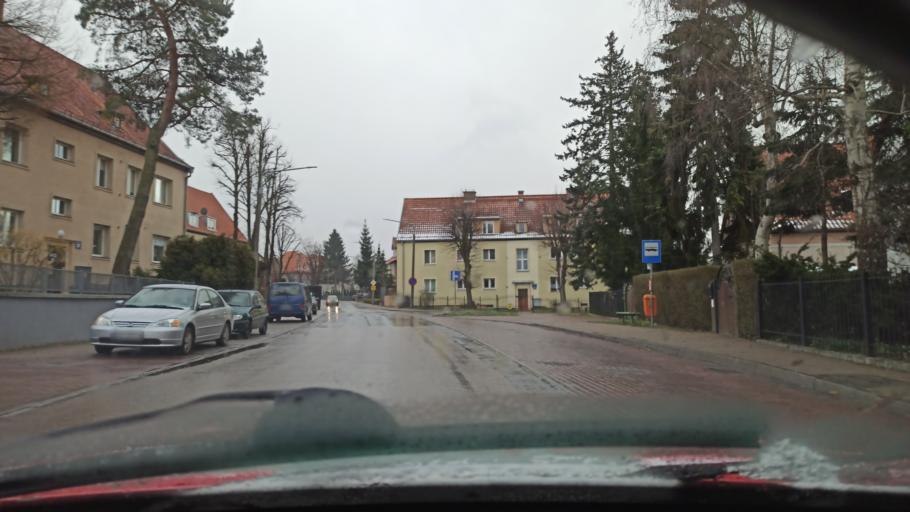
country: PL
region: Warmian-Masurian Voivodeship
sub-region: Powiat elblaski
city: Elblag
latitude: 54.1739
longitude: 19.4126
